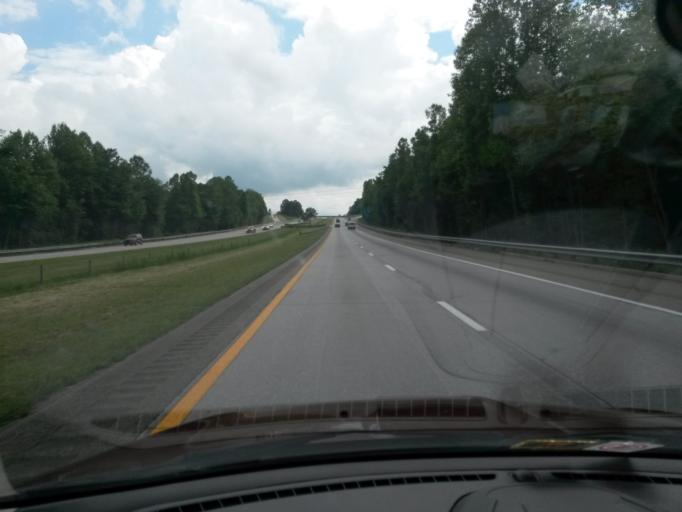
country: US
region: North Carolina
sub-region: Surry County
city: Elkin
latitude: 36.2880
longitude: -80.8175
